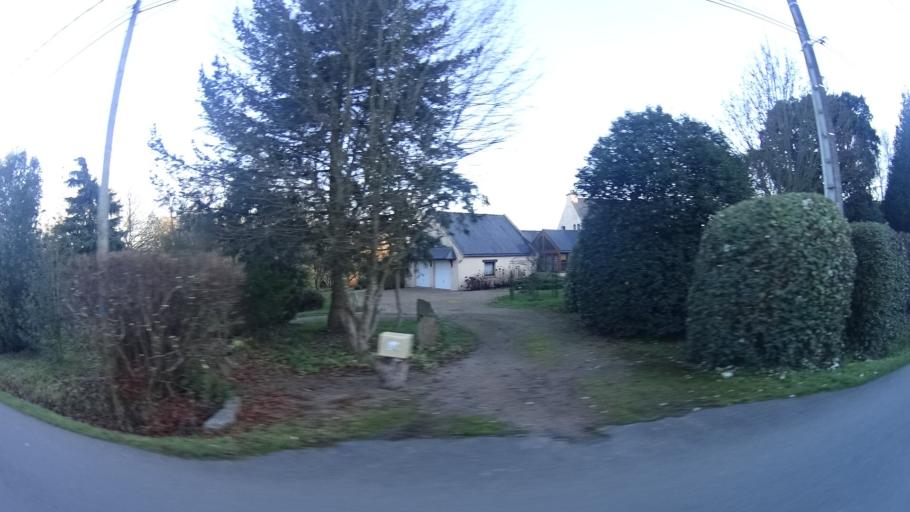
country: FR
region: Brittany
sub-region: Departement du Morbihan
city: Saint-Jean-la-Poterie
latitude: 47.6506
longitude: -2.1255
